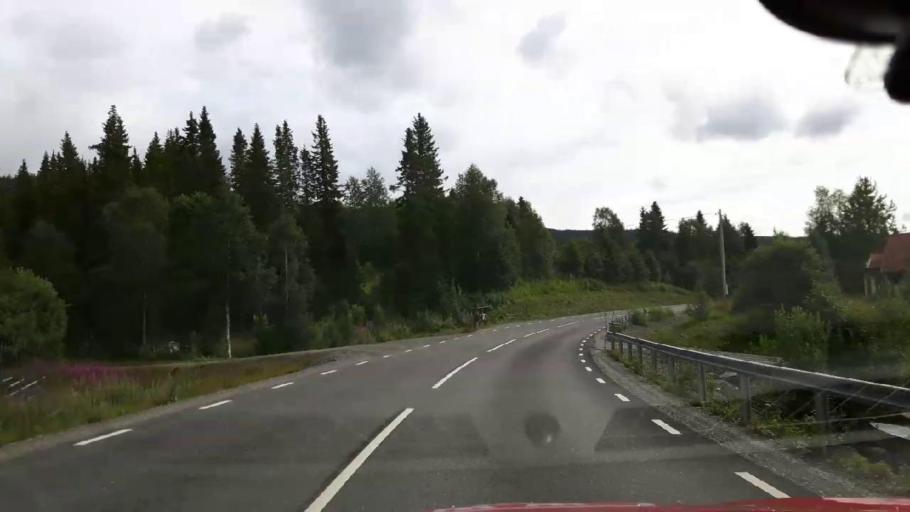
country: NO
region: Nord-Trondelag
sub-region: Lierne
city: Sandvika
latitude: 64.6507
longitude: 14.1372
